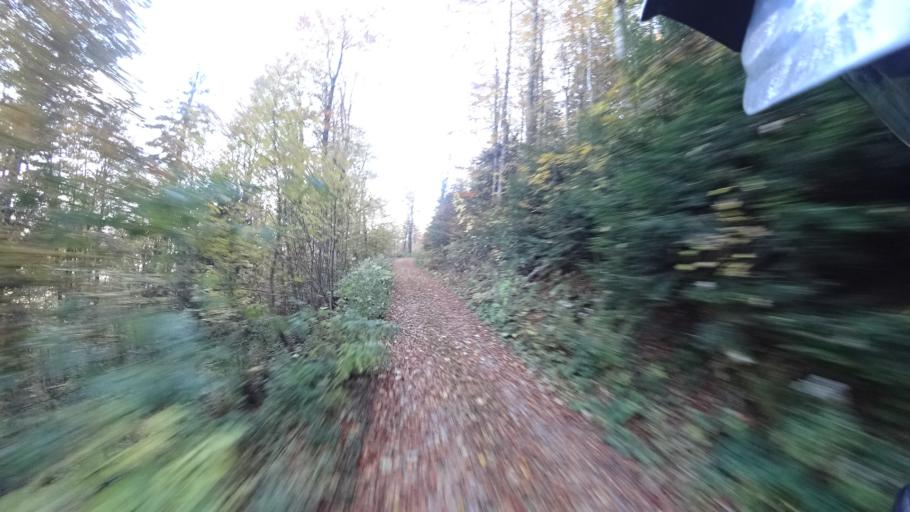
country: HR
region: Karlovacka
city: Plaski
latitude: 45.0127
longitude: 15.3861
